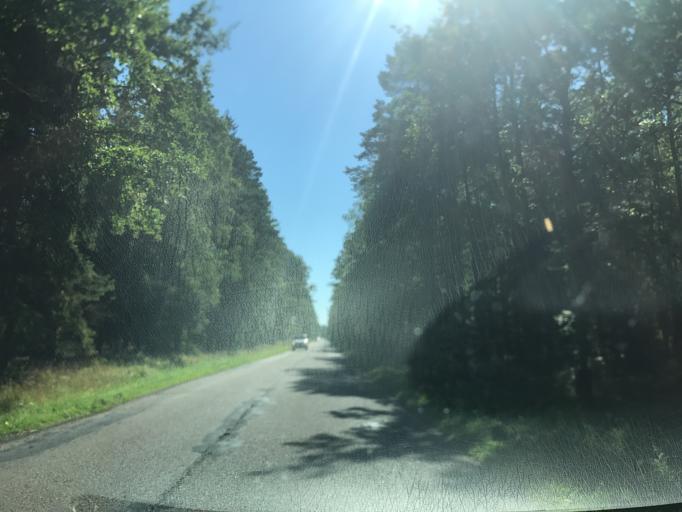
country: PL
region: Pomeranian Voivodeship
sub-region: Powiat bytowski
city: Czarna Dabrowka
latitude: 54.3435
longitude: 17.5991
